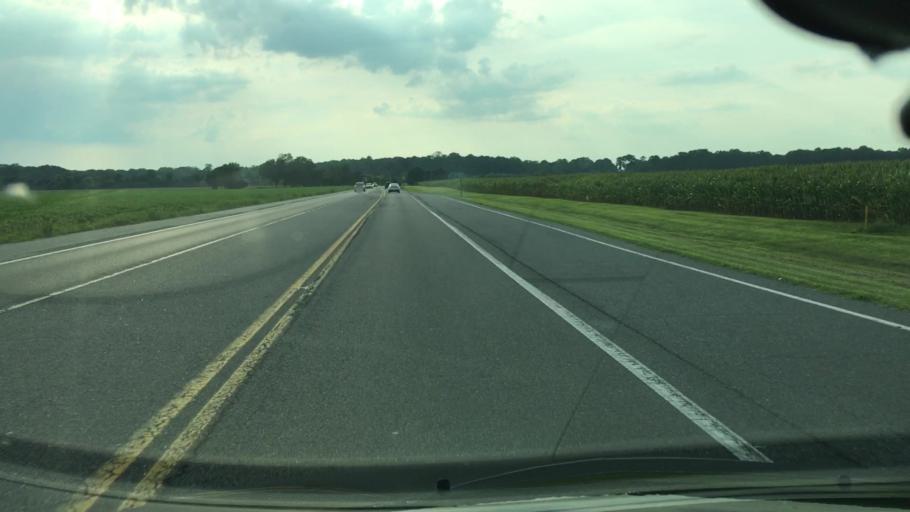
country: US
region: Maryland
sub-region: Worcester County
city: Ocean Pines
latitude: 38.3863
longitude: -75.1962
